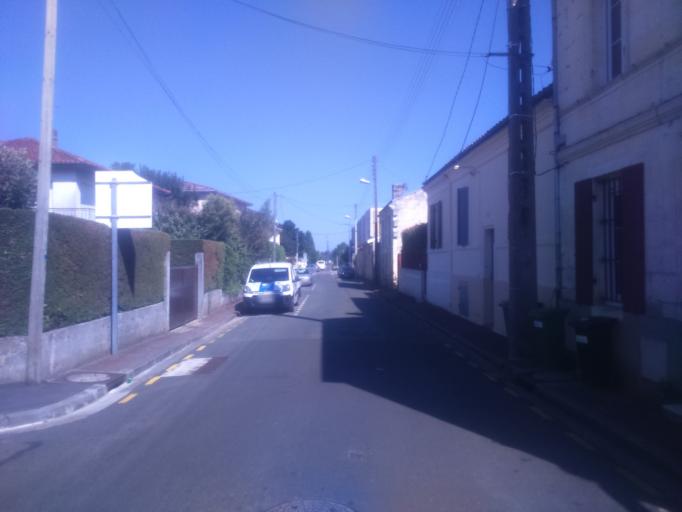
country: FR
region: Aquitaine
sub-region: Departement de la Gironde
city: Lormont
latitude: 44.8772
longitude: -0.5231
